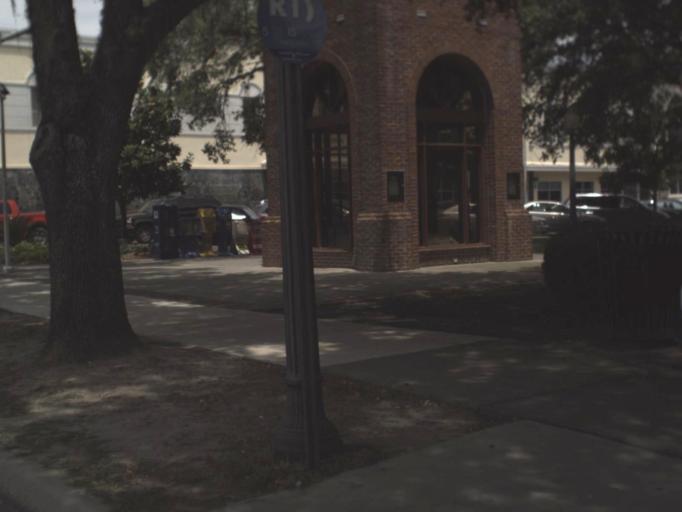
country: US
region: Florida
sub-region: Alachua County
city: Gainesville
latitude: 29.6520
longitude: -82.3236
